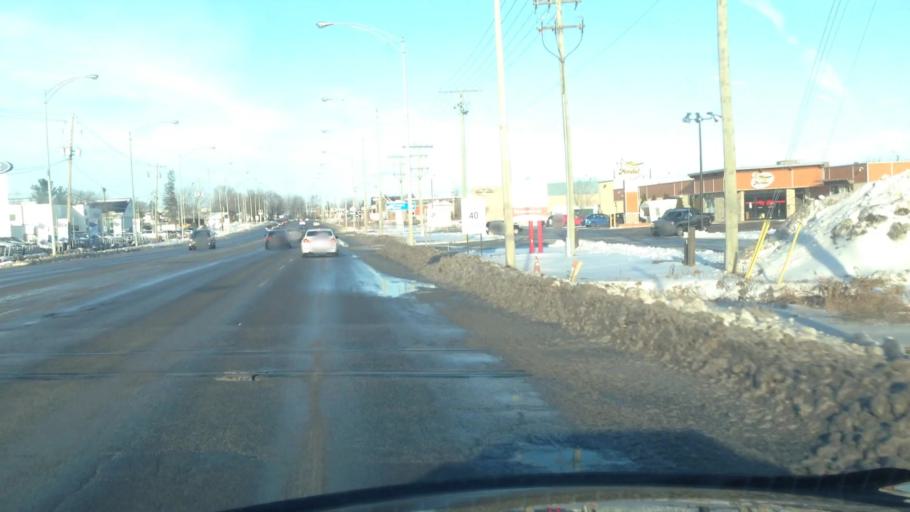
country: CA
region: Quebec
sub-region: Laurentides
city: Saint-Jerome
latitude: 45.7544
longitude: -73.9970
